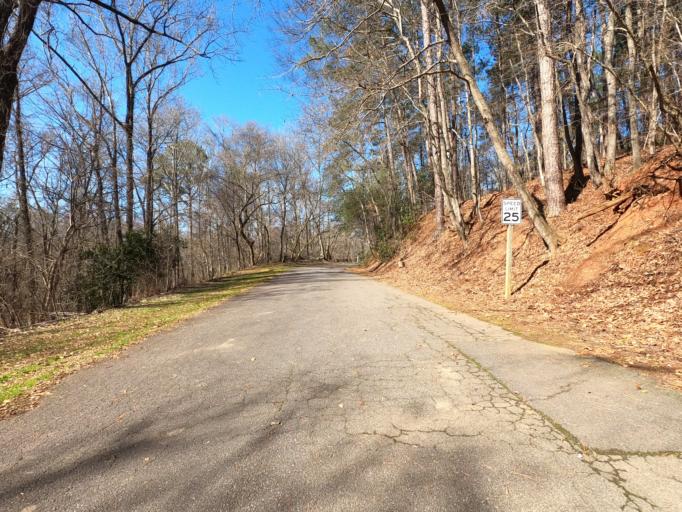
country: US
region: Georgia
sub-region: Clarke County
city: Athens
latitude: 33.9819
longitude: -83.3823
